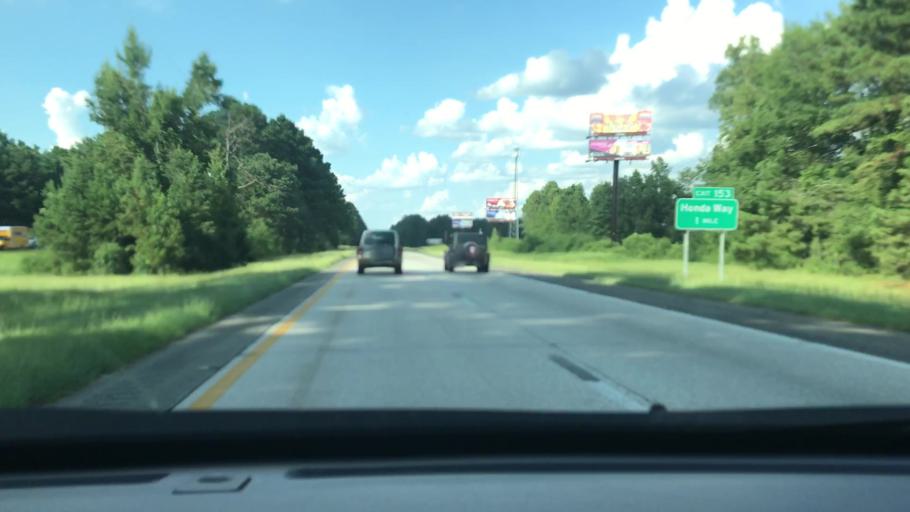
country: US
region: South Carolina
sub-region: Florence County
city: Timmonsville
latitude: 34.1007
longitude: -79.9226
